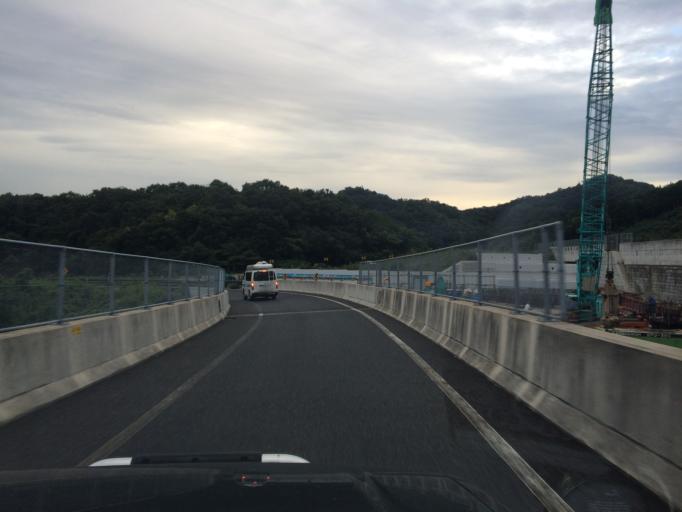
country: JP
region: Tottori
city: Tottori
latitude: 35.4803
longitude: 134.1977
